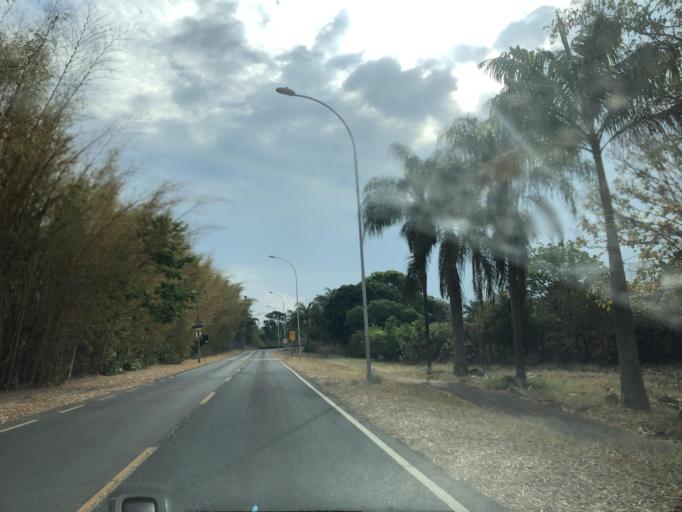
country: BR
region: Federal District
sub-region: Brasilia
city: Brasilia
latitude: -15.9440
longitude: -47.9845
